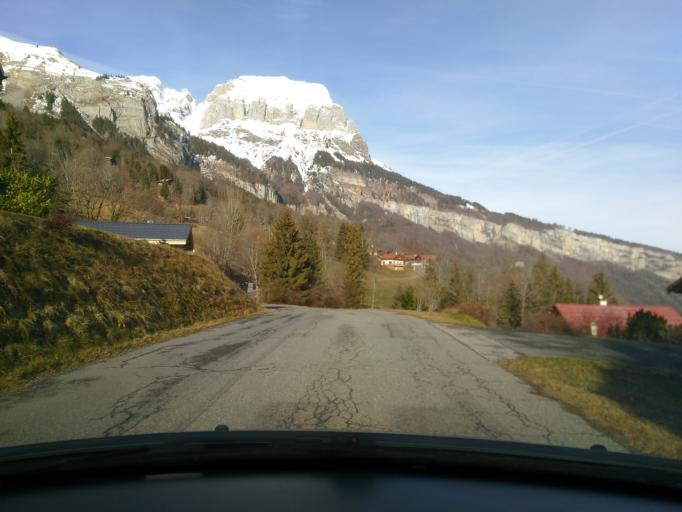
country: FR
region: Rhone-Alpes
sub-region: Departement de la Haute-Savoie
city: Sallanches
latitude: 45.9548
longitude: 6.6132
